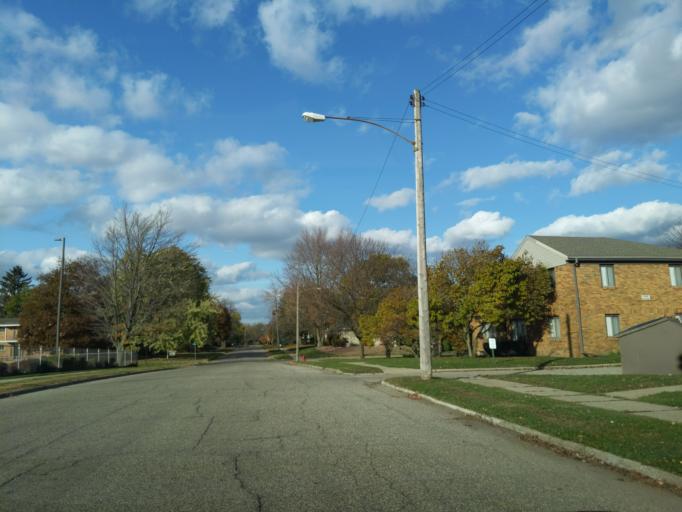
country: US
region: Michigan
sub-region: Ingham County
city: East Lansing
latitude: 42.7449
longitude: -84.5153
